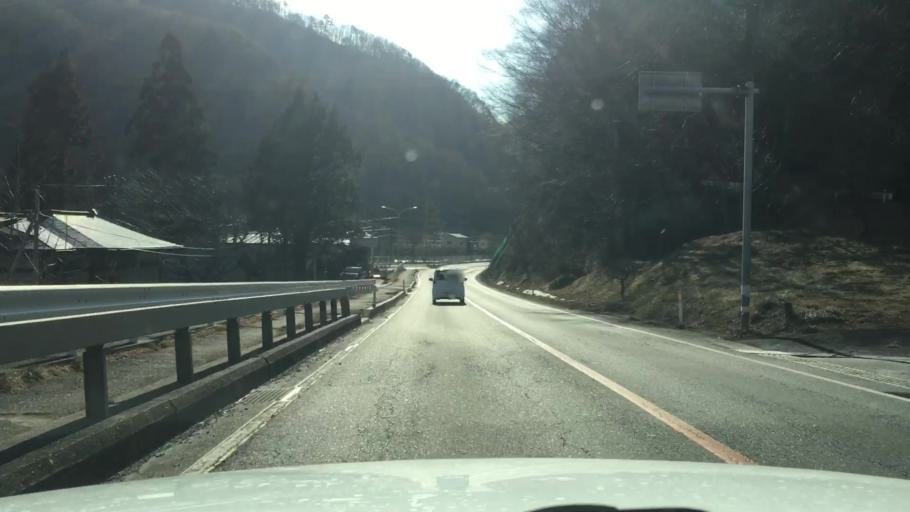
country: JP
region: Iwate
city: Miyako
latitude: 39.5945
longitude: 141.6759
